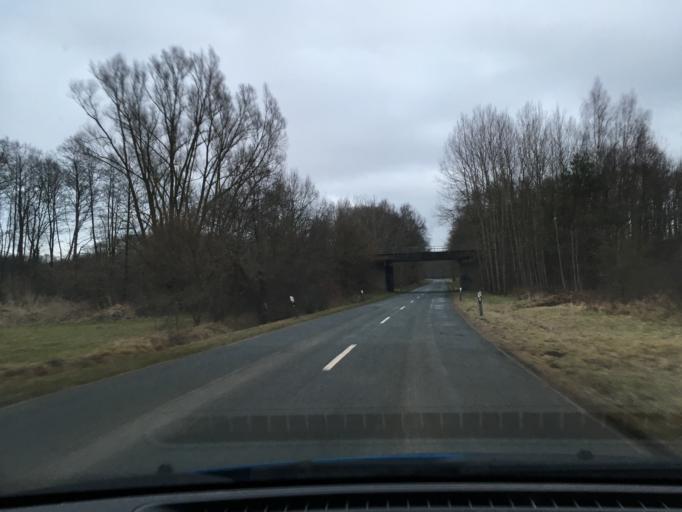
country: DE
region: Lower Saxony
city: Scharnebeck
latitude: 53.3130
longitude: 10.4962
